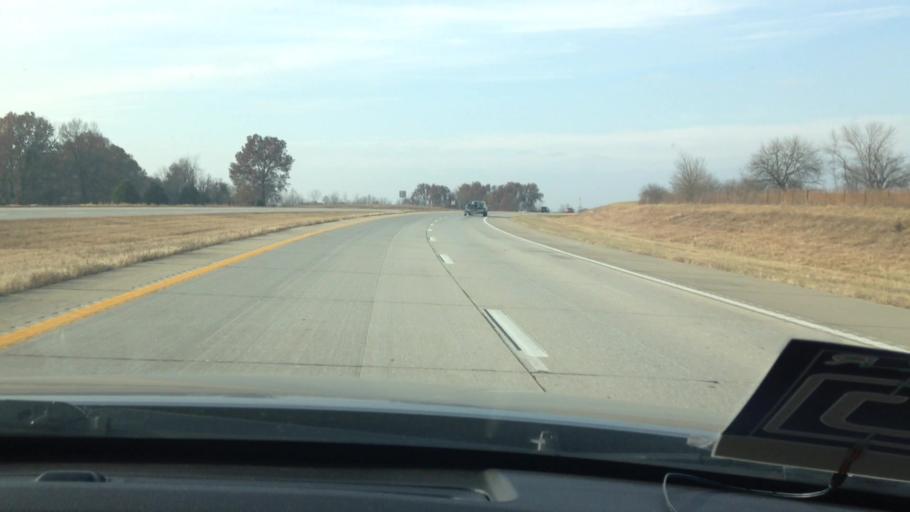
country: US
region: Missouri
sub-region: Henry County
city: Clinton
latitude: 38.4425
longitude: -93.9528
